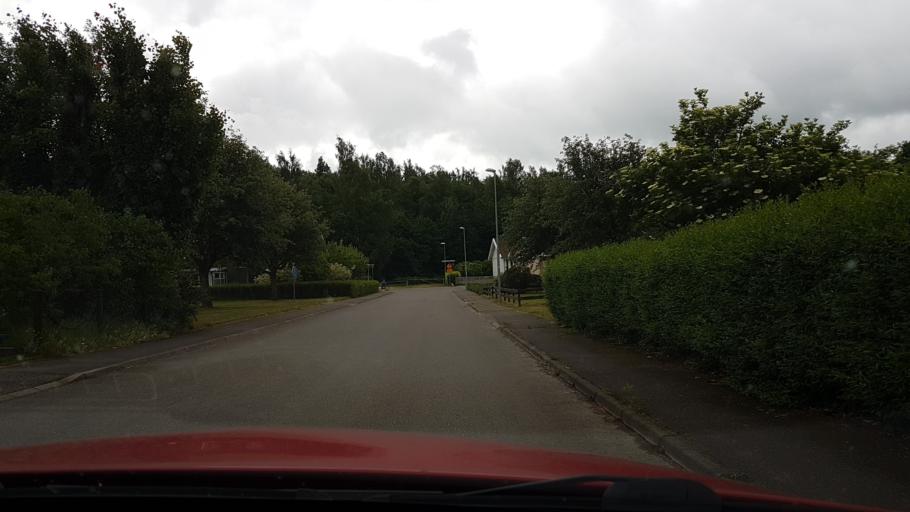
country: SE
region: Vaestra Goetaland
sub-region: Skovde Kommun
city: Skultorp
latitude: 58.3650
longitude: 13.8251
